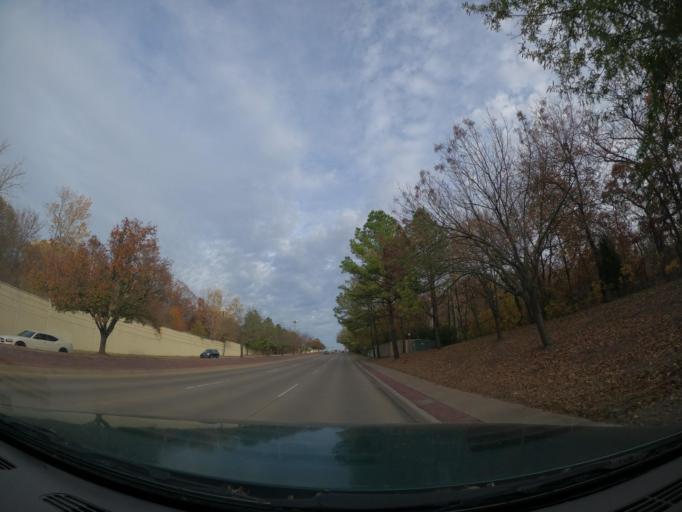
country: US
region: Oklahoma
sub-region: Tulsa County
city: Jenks
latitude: 36.0608
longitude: -95.9269
